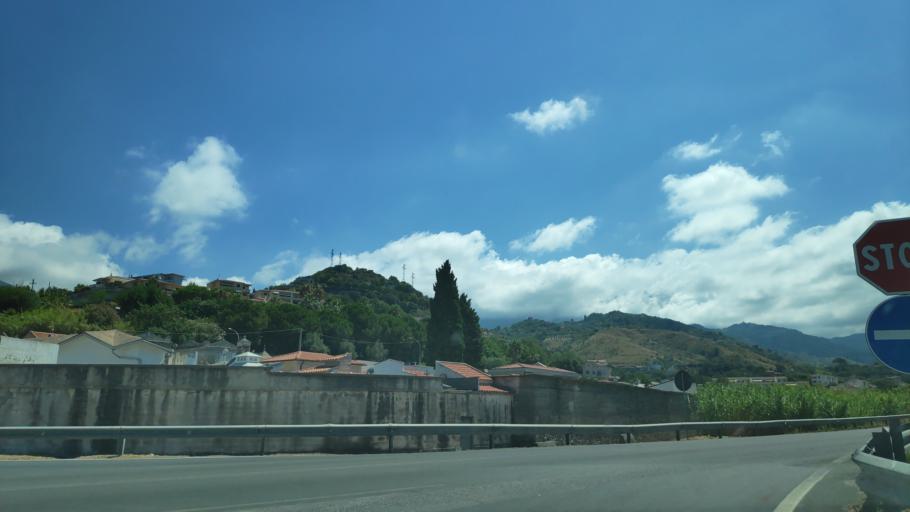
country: IT
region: Calabria
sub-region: Provincia di Cosenza
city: Diamante
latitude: 39.6783
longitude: 15.8231
